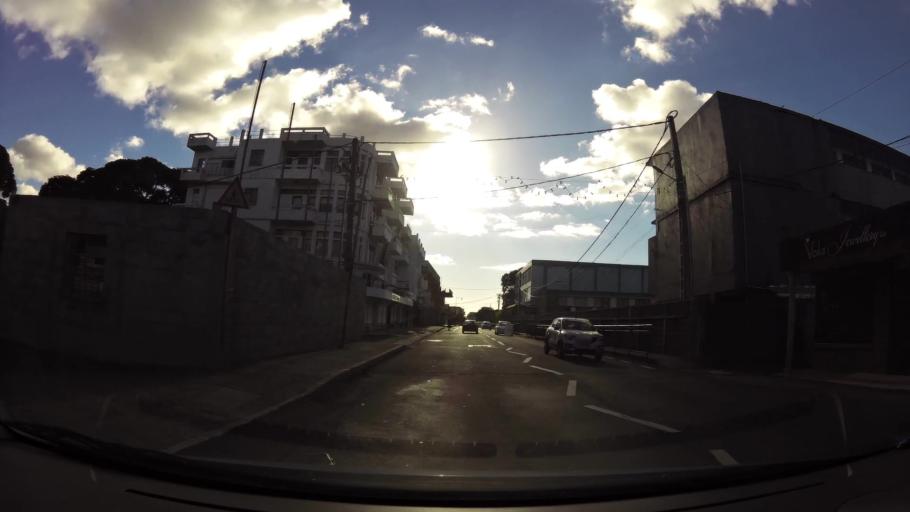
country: MU
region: Plaines Wilhems
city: Ebene
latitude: -20.2462
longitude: 57.4795
